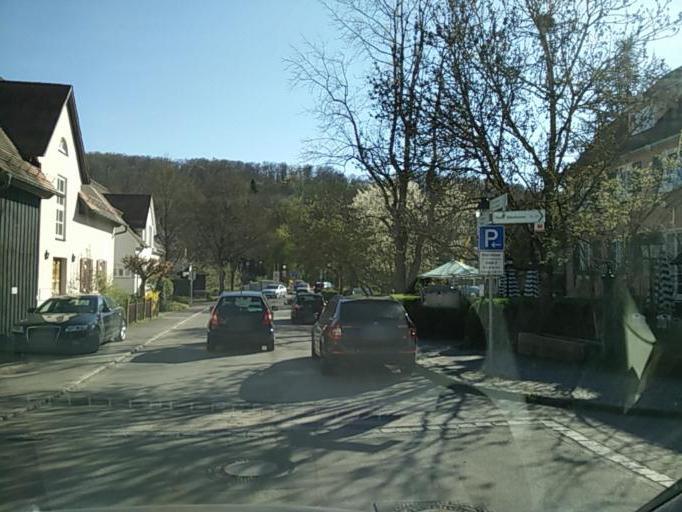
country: DE
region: Baden-Wuerttemberg
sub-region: Tuebingen Region
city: Tuebingen
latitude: 48.5596
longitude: 9.0610
